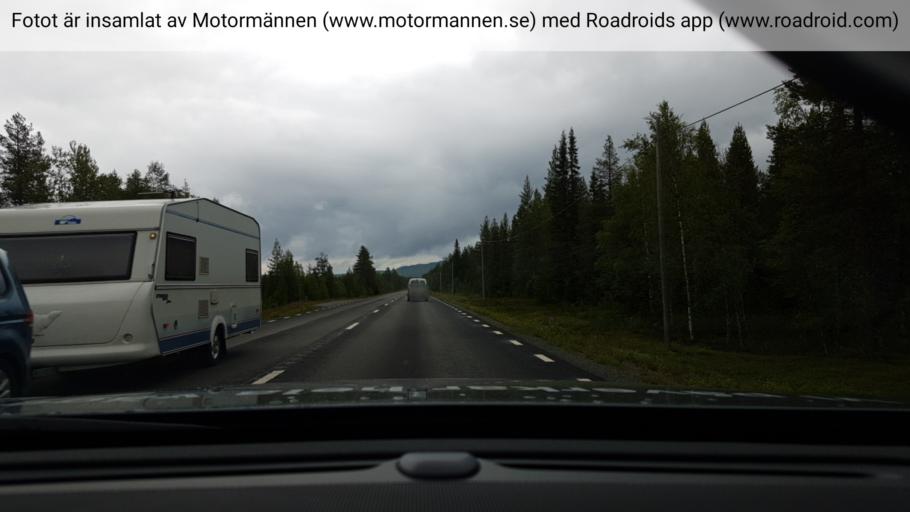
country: SE
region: Vaesterbotten
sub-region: Norsjo Kommun
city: Norsjoe
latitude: 65.2938
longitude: 19.5670
